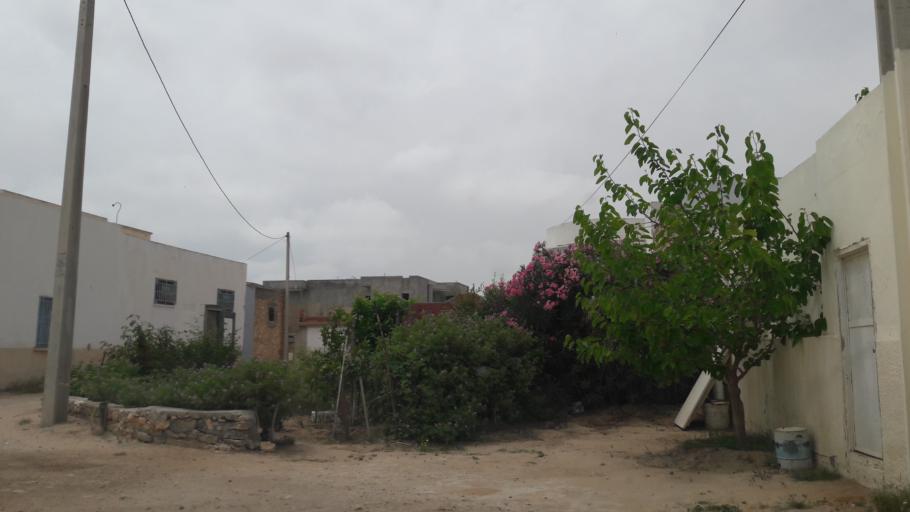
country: TN
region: Safaqis
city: Al Qarmadah
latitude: 34.7926
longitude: 10.7543
